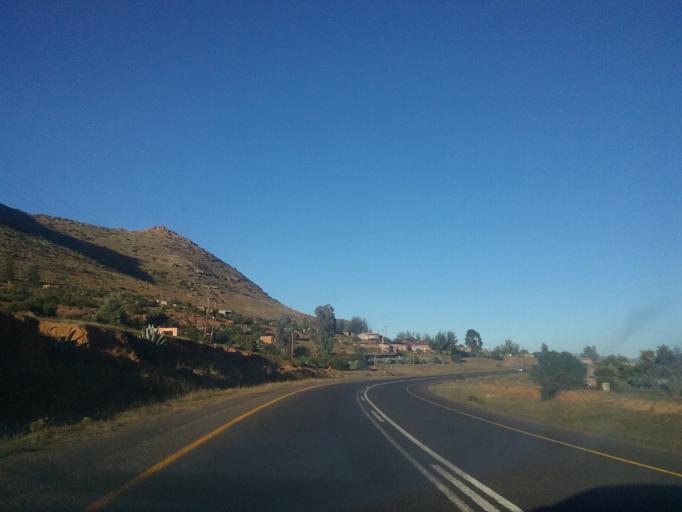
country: LS
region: Mohale's Hoek District
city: Mohale's Hoek
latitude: -30.1786
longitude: 27.4335
